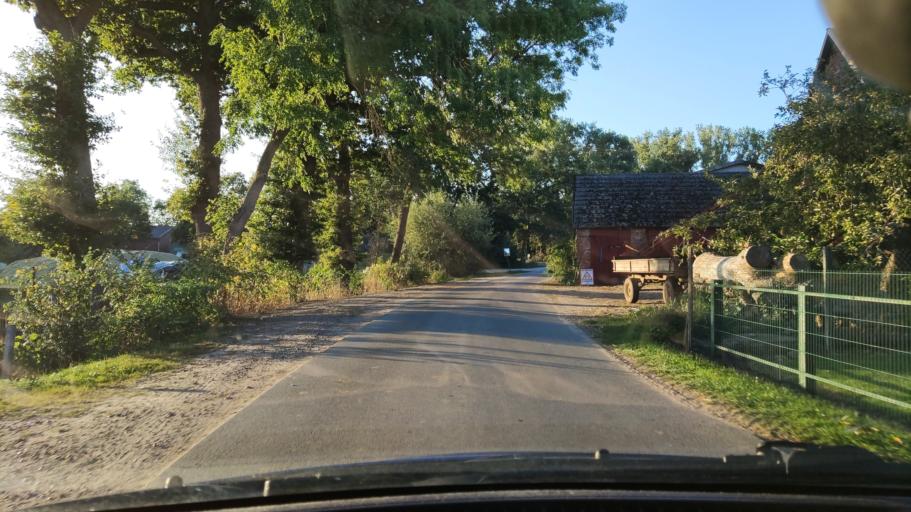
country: DE
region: Lower Saxony
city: Dannenberg
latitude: 53.1208
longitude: 11.0993
